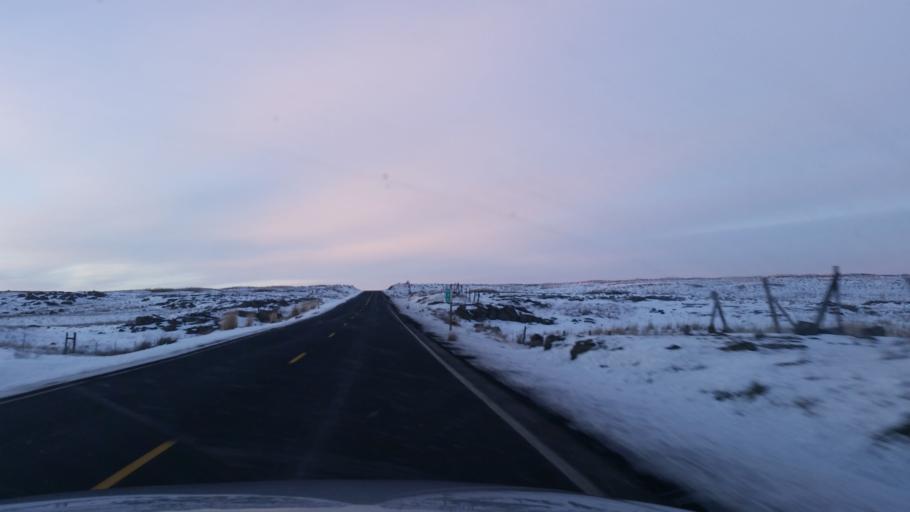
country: US
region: Washington
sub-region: Spokane County
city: Medical Lake
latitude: 47.2183
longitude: -117.8992
